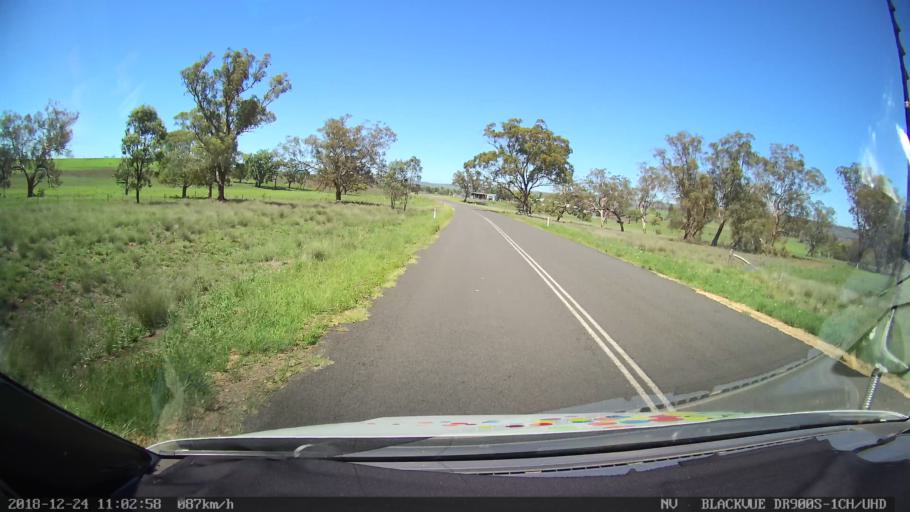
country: AU
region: New South Wales
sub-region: Upper Hunter Shire
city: Merriwa
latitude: -32.0909
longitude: 150.3706
